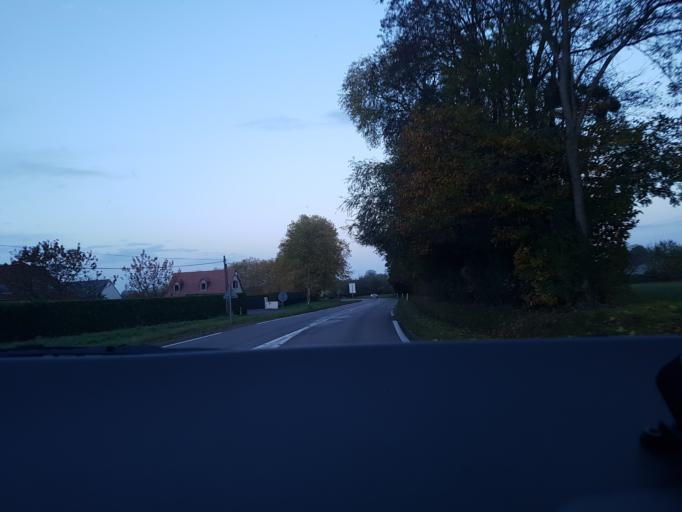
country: FR
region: Haute-Normandie
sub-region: Departement de l'Eure
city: Beuzeville
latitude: 49.3440
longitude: 0.3607
